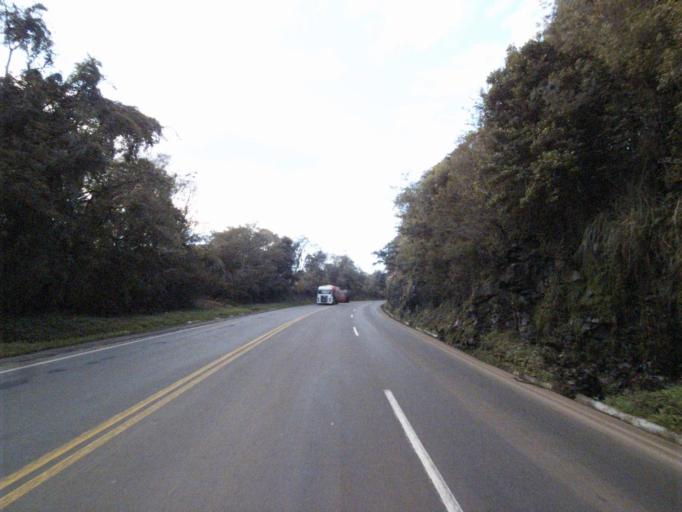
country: BR
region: Santa Catarina
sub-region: Joacaba
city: Joacaba
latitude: -27.2673
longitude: -51.4440
